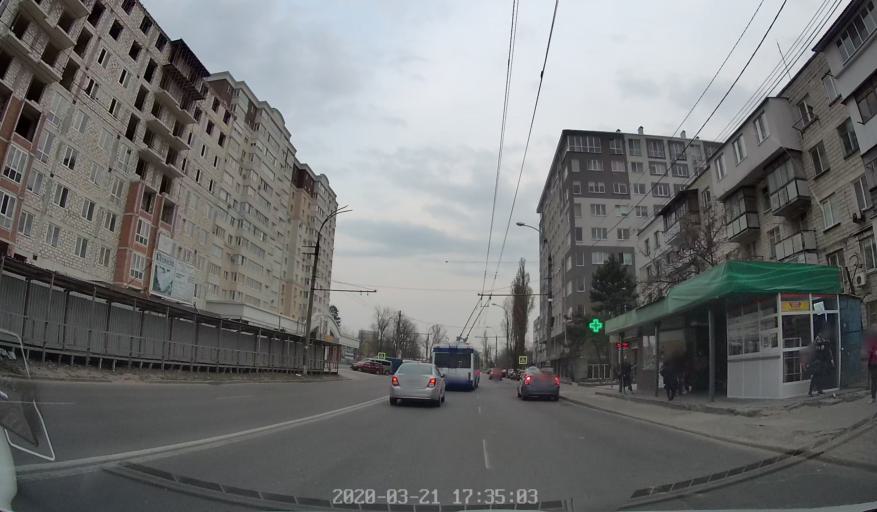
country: MD
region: Chisinau
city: Chisinau
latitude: 46.9971
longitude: 28.8089
